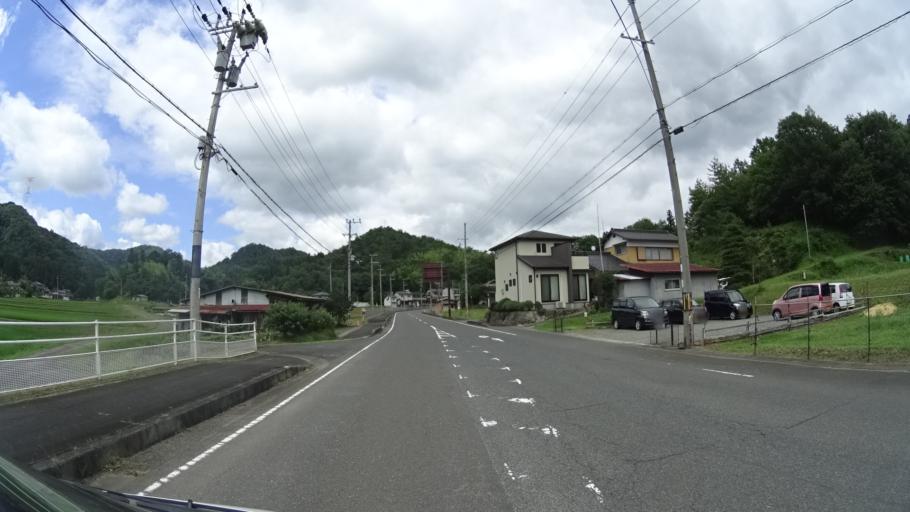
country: JP
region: Kyoto
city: Ayabe
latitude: 35.3266
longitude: 135.2791
